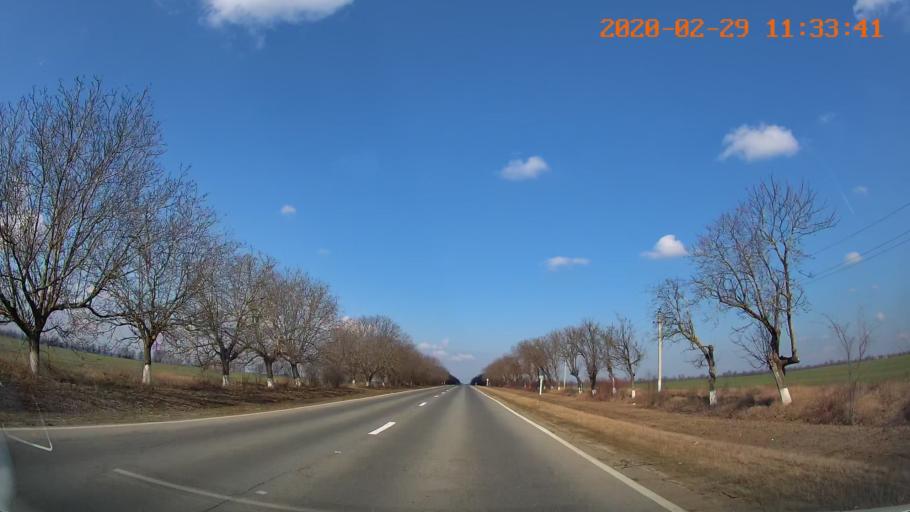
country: MD
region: Rezina
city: Saharna
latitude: 47.5550
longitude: 29.0818
